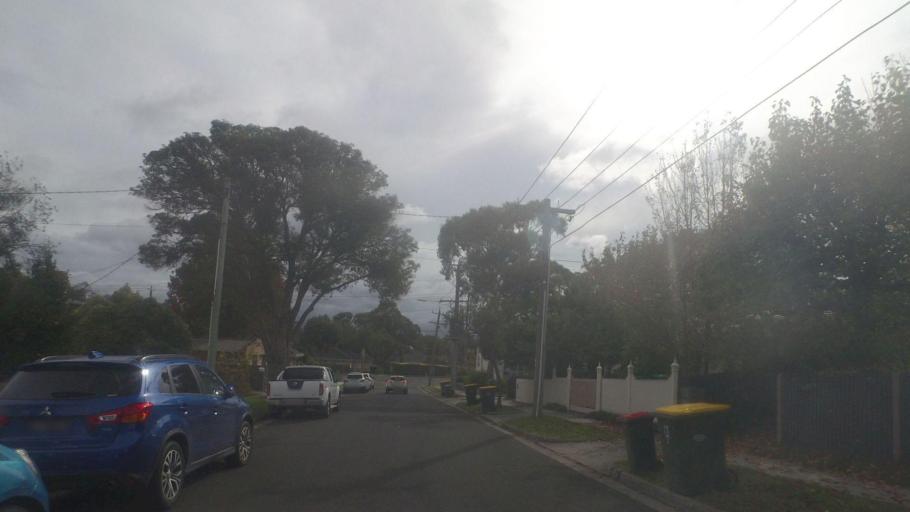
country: AU
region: Victoria
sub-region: Whitehorse
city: Blackburn South
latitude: -37.8320
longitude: 145.1436
